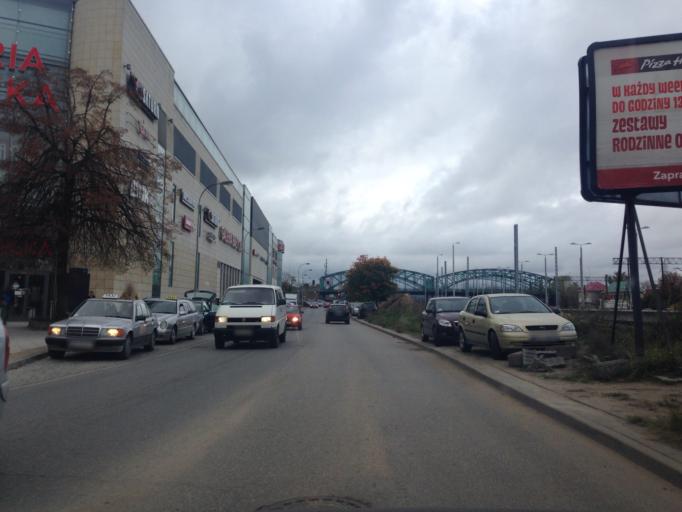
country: PL
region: Pomeranian Voivodeship
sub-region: Gdansk
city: Gdansk
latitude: 54.3823
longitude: 18.6031
